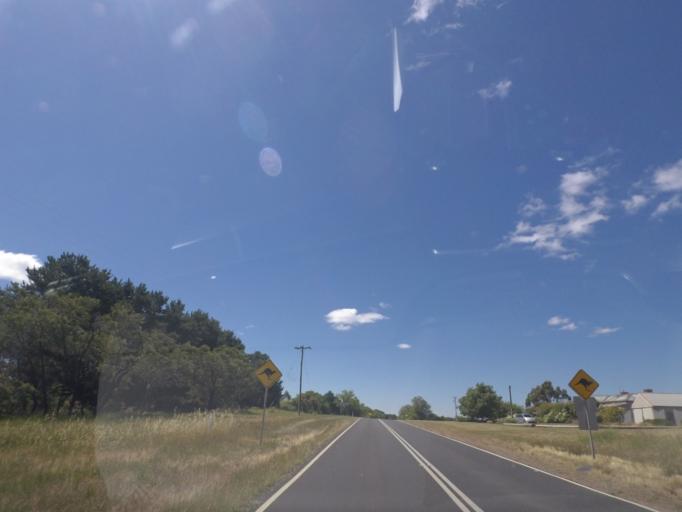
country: AU
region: Victoria
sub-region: Mount Alexander
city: Castlemaine
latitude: -37.2412
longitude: 144.3260
